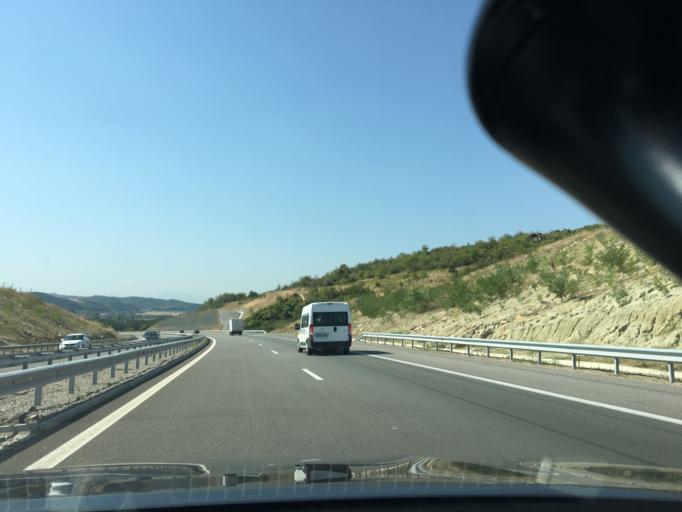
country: BG
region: Kyustendil
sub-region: Obshtina Dupnitsa
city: Dupnitsa
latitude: 42.2478
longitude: 23.0851
